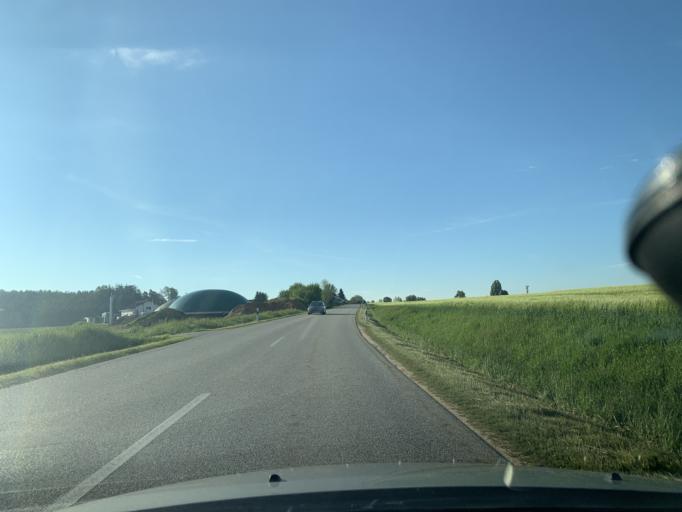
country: DE
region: Bavaria
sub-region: Lower Bavaria
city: Adlkofen
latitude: 48.5255
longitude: 12.2829
